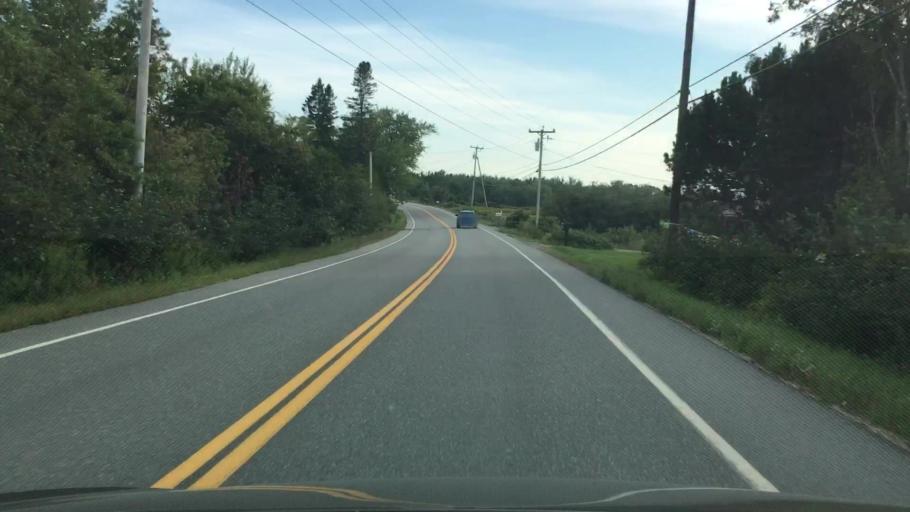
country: US
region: Maine
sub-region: Hancock County
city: Penobscot
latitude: 44.4728
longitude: -68.7806
